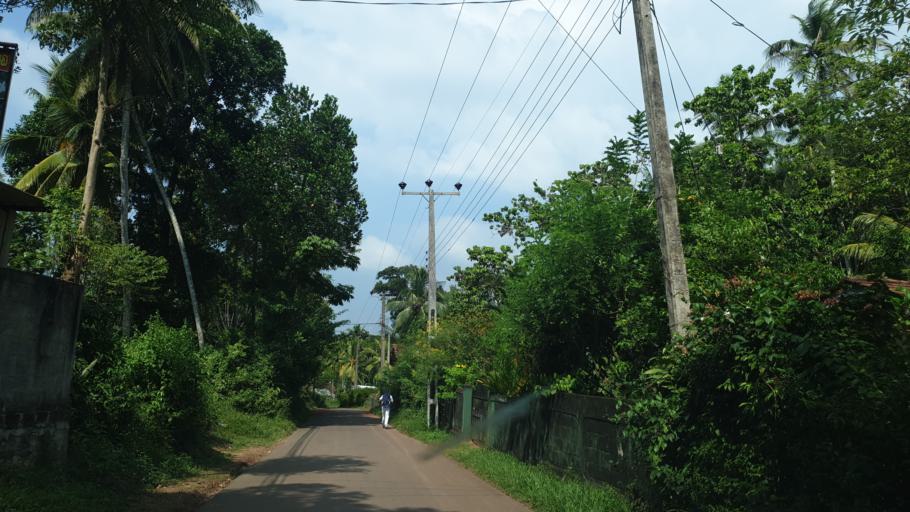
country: LK
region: Western
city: Panadura
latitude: 6.7259
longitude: 79.9539
